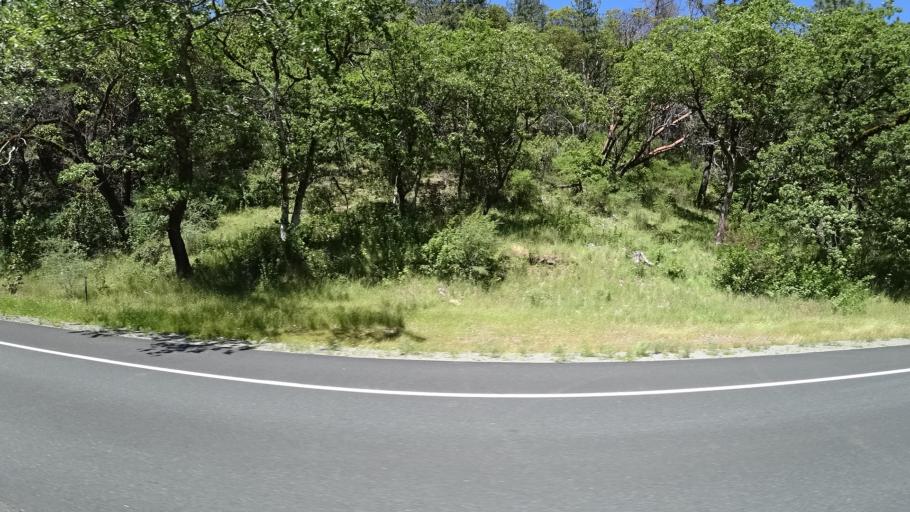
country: US
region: California
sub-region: Humboldt County
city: Willow Creek
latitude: 40.7905
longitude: -123.4378
